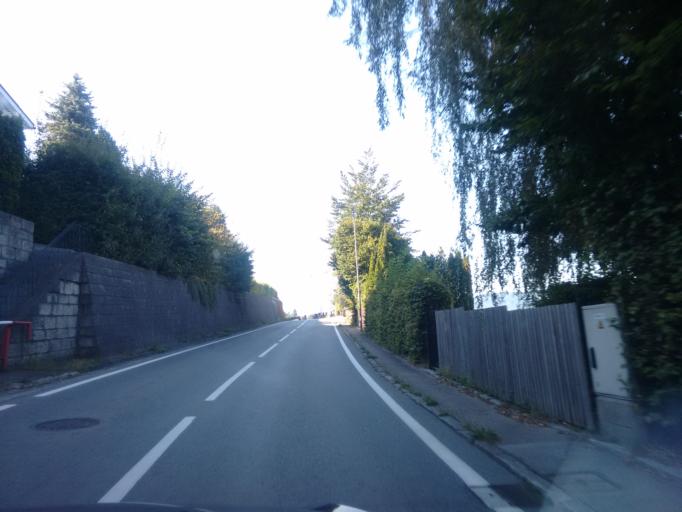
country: AT
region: Upper Austria
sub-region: Politischer Bezirk Vocklabruck
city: Attersee
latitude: 47.9138
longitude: 13.5769
